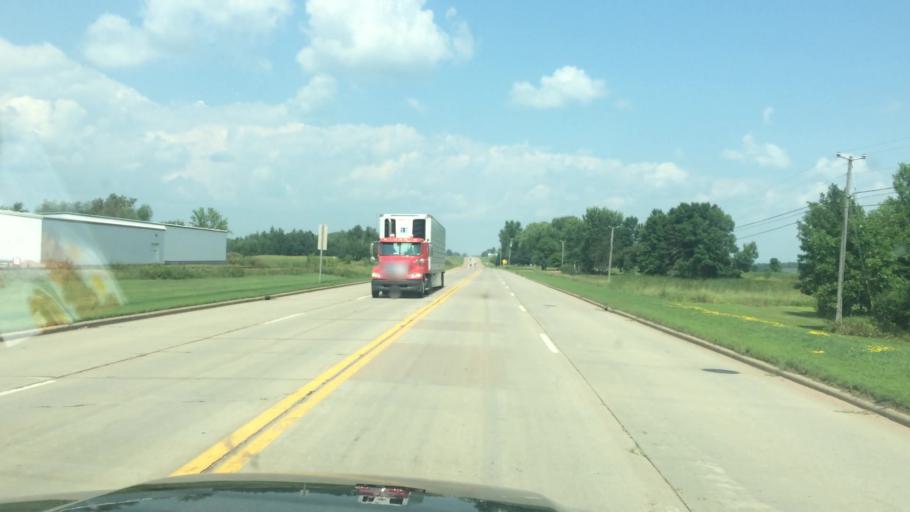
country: US
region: Wisconsin
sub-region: Clark County
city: Colby
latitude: 44.8530
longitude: -90.3160
